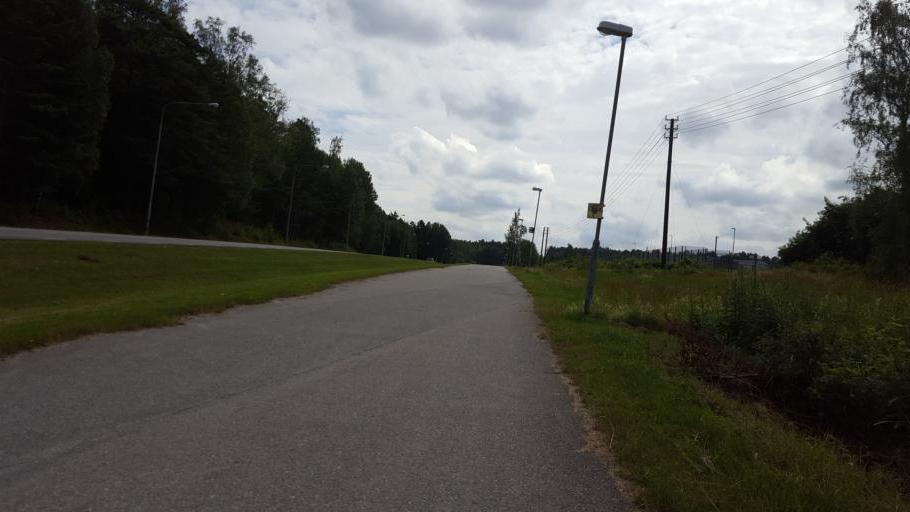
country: SE
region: Stockholm
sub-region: Upplands Vasby Kommun
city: Upplands Vaesby
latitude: 59.5119
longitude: 17.8991
